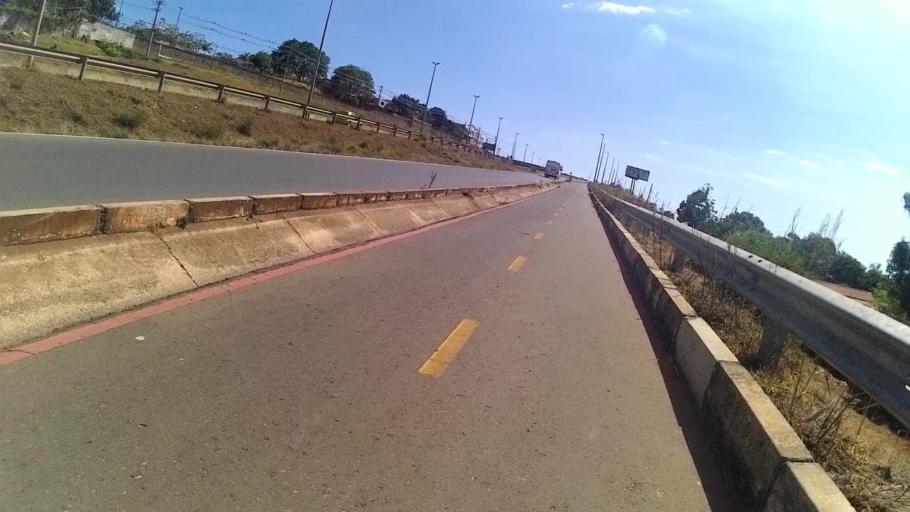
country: BR
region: Federal District
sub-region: Brasilia
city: Brasilia
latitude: -15.6755
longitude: -47.8433
